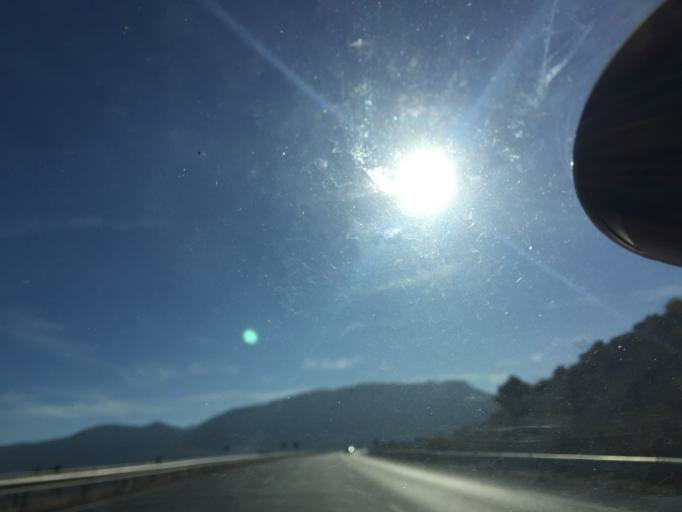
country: ES
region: Andalusia
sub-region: Provincia de Jaen
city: La Guardia de Jaen
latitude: 37.7599
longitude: -3.7091
